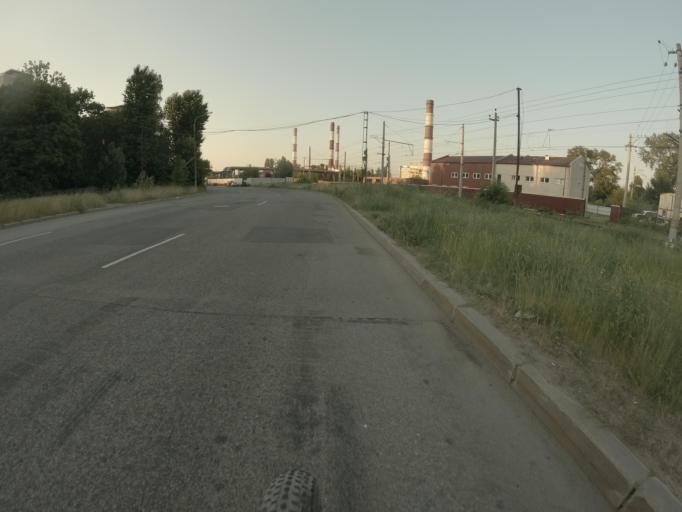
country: RU
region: St.-Petersburg
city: Avtovo
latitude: 59.8665
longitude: 30.2795
